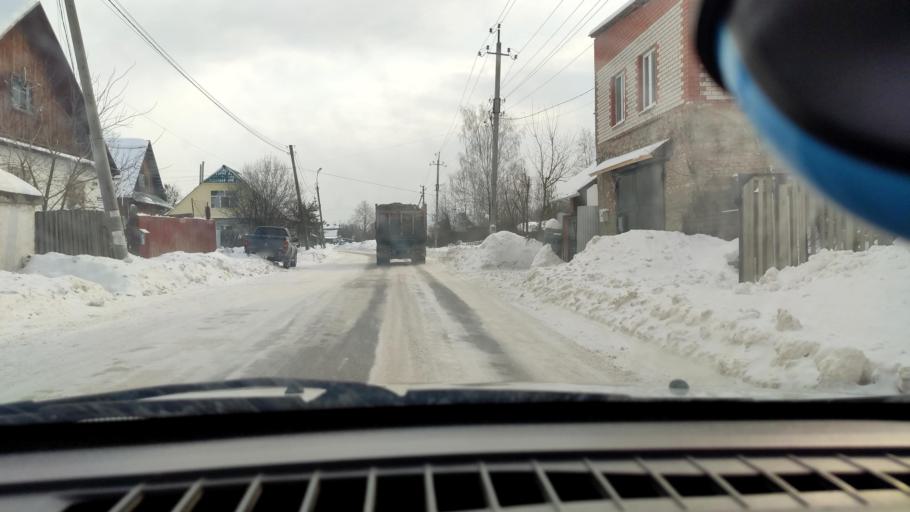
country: RU
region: Perm
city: Overyata
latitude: 58.0938
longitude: 55.8553
